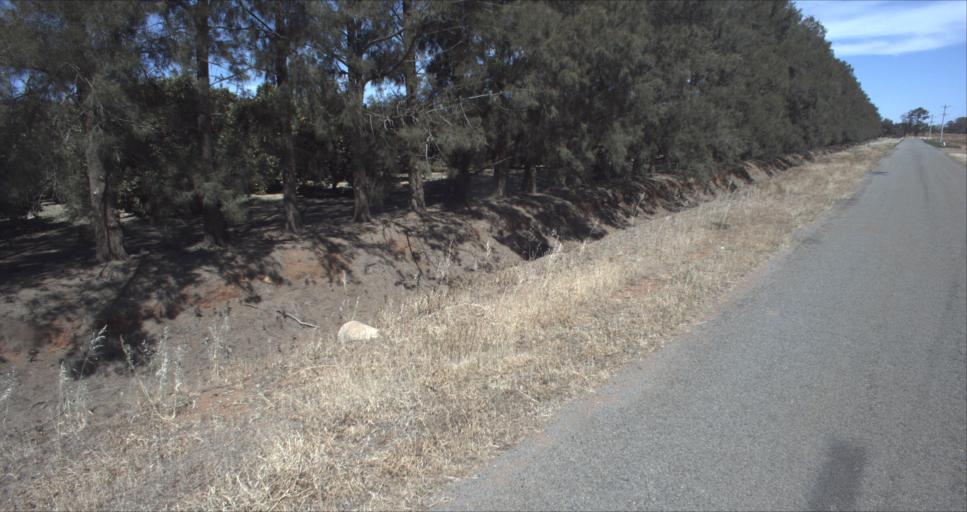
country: AU
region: New South Wales
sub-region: Leeton
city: Leeton
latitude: -34.6032
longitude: 146.4341
